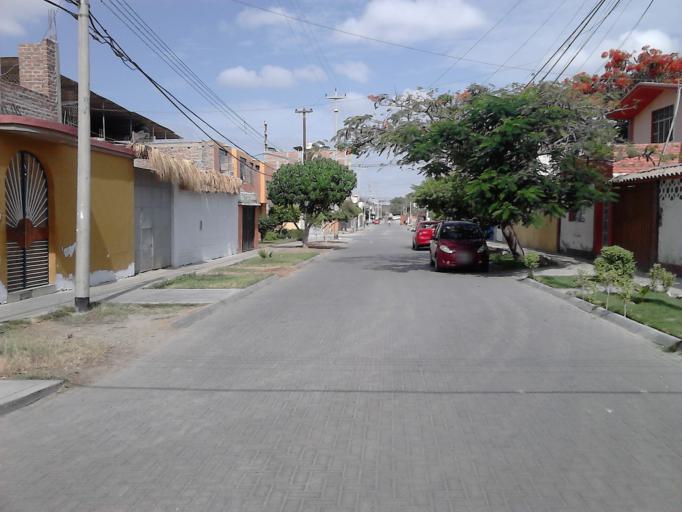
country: PE
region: Piura
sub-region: Provincia de Piura
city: Piura
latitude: -5.1901
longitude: -80.6449
